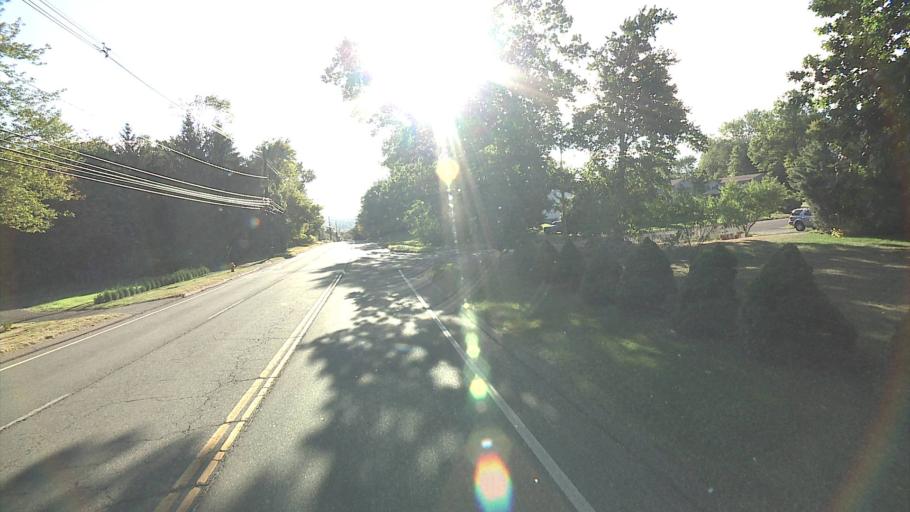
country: US
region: Connecticut
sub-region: New Haven County
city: Wallingford
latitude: 41.4931
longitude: -72.8357
